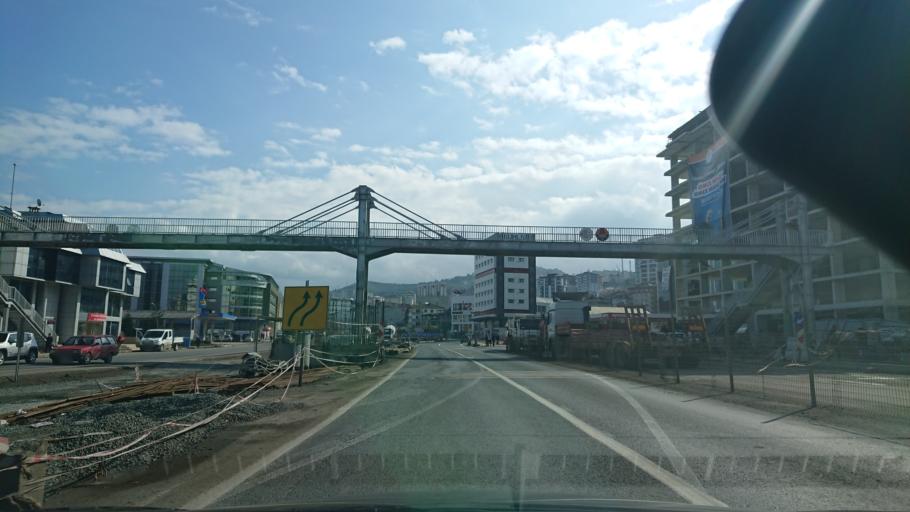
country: TR
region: Trabzon
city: Yomra
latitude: 40.9653
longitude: 39.8373
